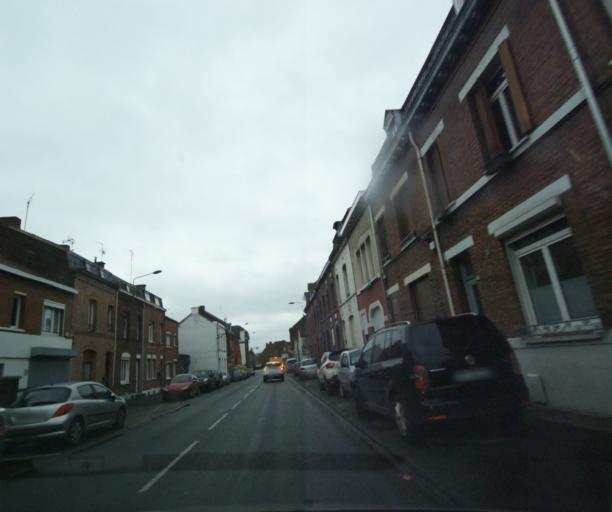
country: FR
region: Nord-Pas-de-Calais
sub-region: Departement du Nord
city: Anzin
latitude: 50.3643
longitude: 3.5073
